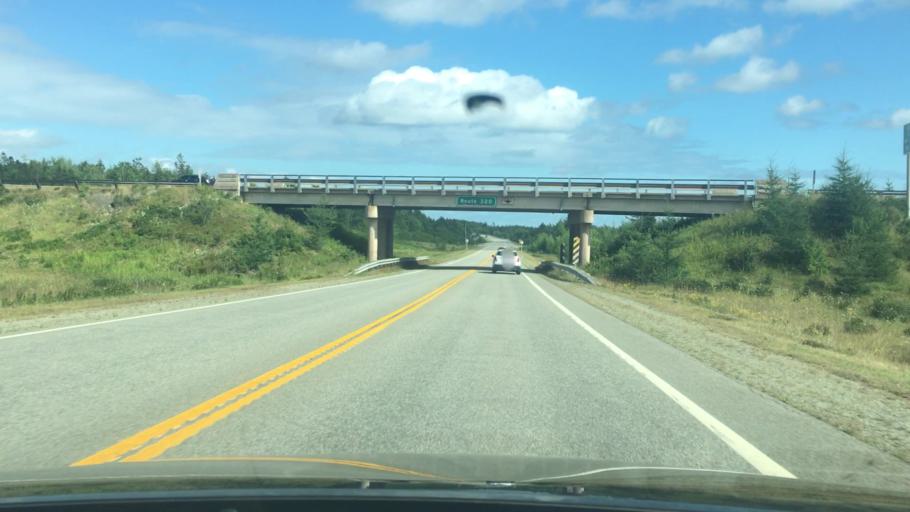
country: CA
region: Nova Scotia
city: Princeville
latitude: 45.6129
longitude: -61.0825
